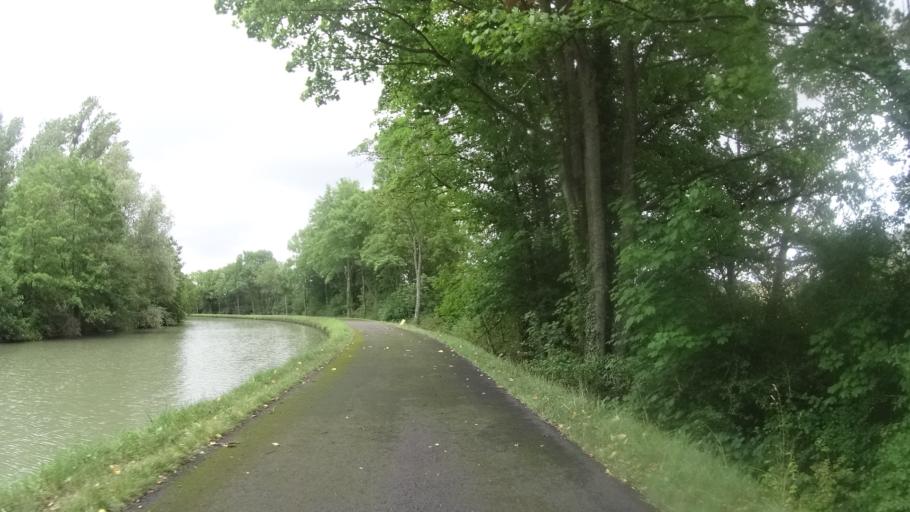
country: FR
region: Lorraine
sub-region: Departement de Meurthe-et-Moselle
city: Einville-au-Jard
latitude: 48.6499
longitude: 6.4617
